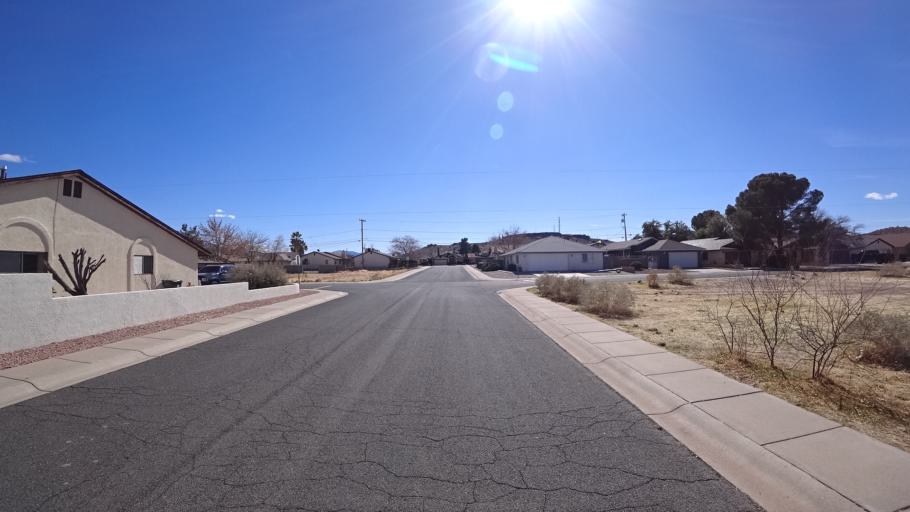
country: US
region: Arizona
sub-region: Mohave County
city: Kingman
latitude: 35.2078
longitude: -114.0379
